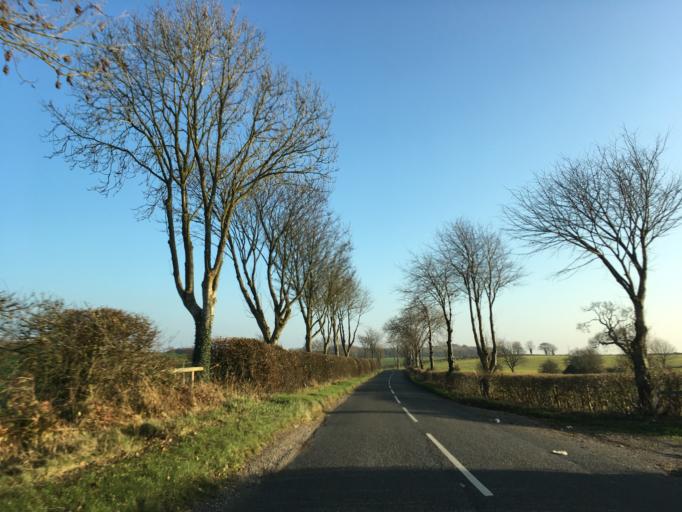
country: GB
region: England
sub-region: Wiltshire
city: Luckington
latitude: 51.5658
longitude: -2.2950
